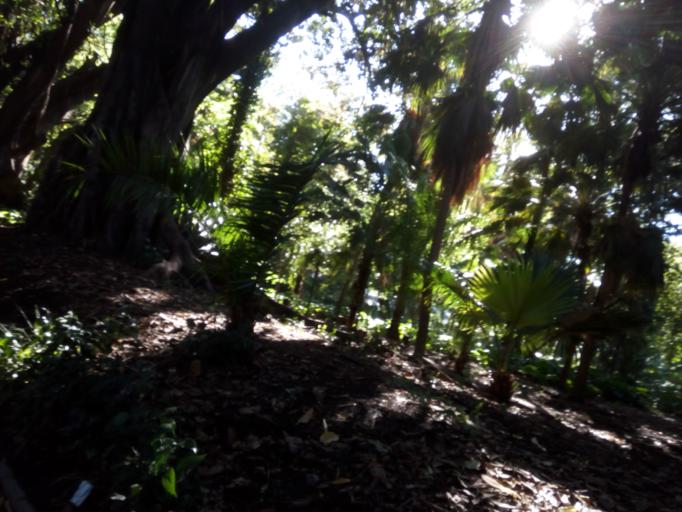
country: DZ
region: Alger
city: Algiers
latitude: 36.7466
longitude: 3.0762
